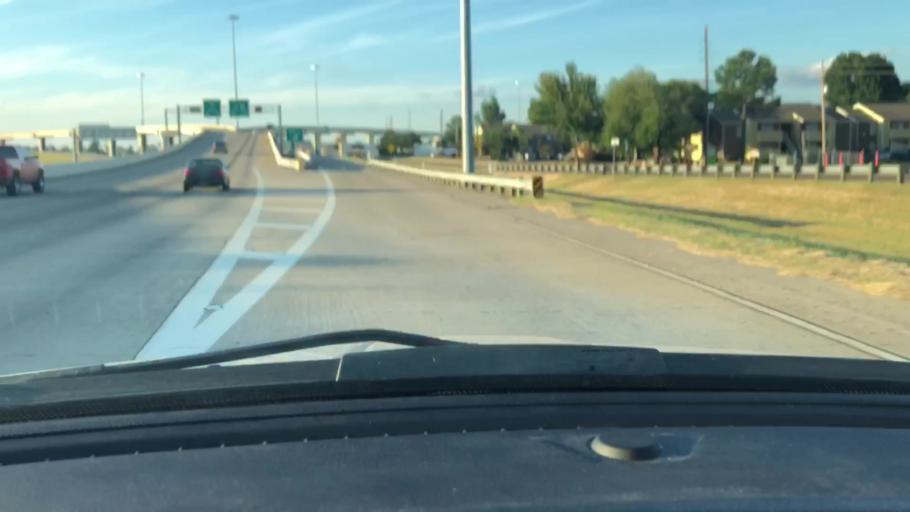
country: US
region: Texas
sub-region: Bowie County
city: Wake Village
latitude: 33.4476
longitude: -94.0966
